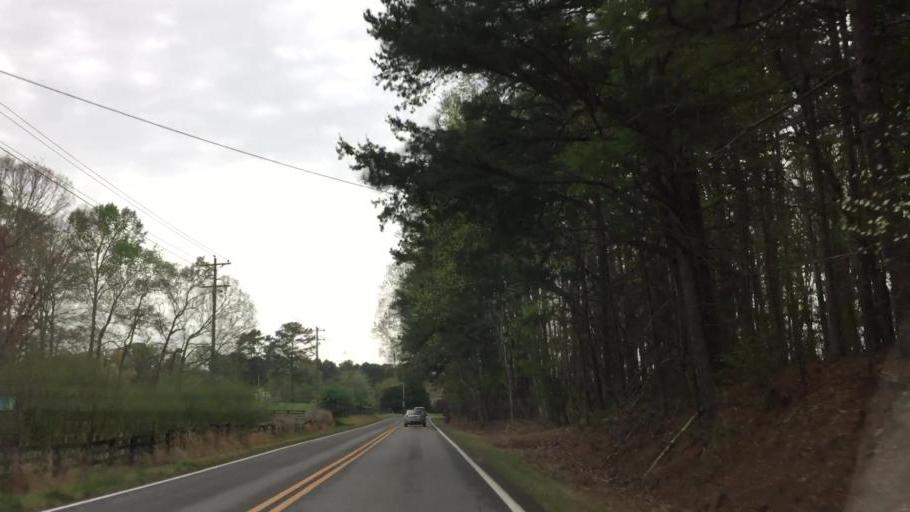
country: US
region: Georgia
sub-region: Fulton County
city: Milton
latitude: 34.1820
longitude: -84.3400
